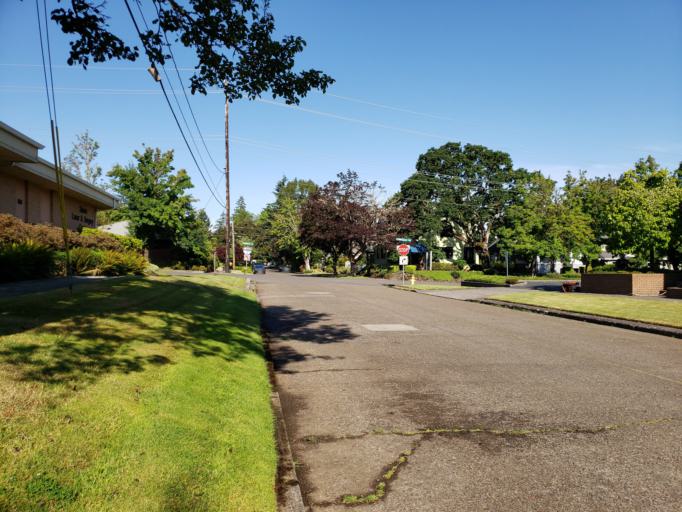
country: US
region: Oregon
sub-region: Marion County
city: Salem
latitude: 44.9282
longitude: -123.0437
